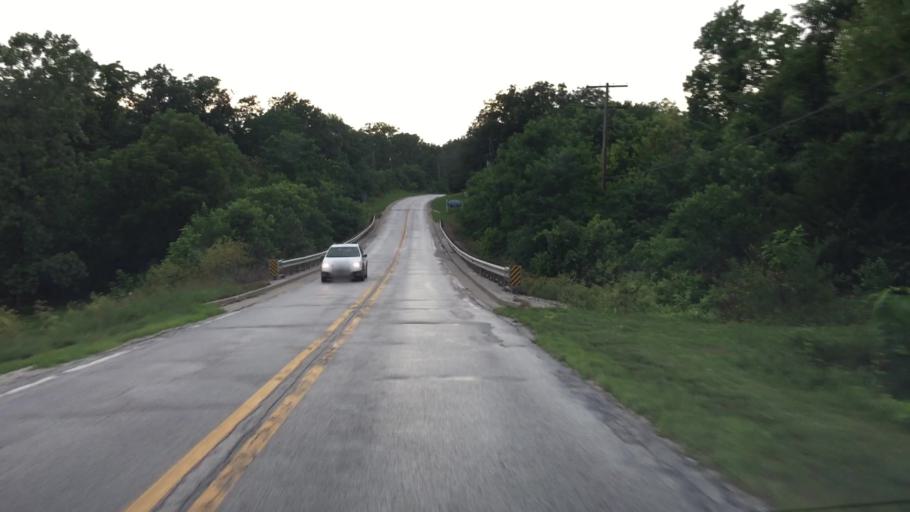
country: US
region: Illinois
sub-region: Hancock County
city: Warsaw
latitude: 40.3566
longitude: -91.4235
